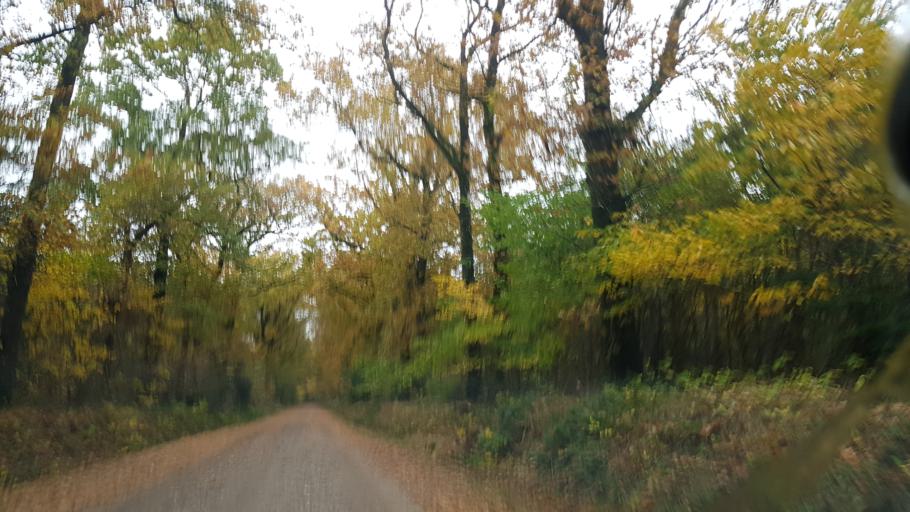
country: DK
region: South Denmark
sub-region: Tonder Kommune
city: Sherrebek
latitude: 55.1789
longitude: 8.7654
